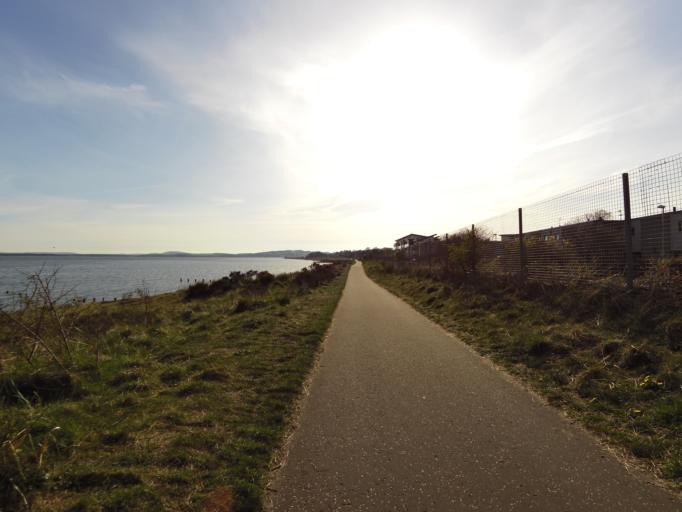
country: GB
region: Scotland
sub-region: Fife
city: Tayport
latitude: 56.4767
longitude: -2.8311
